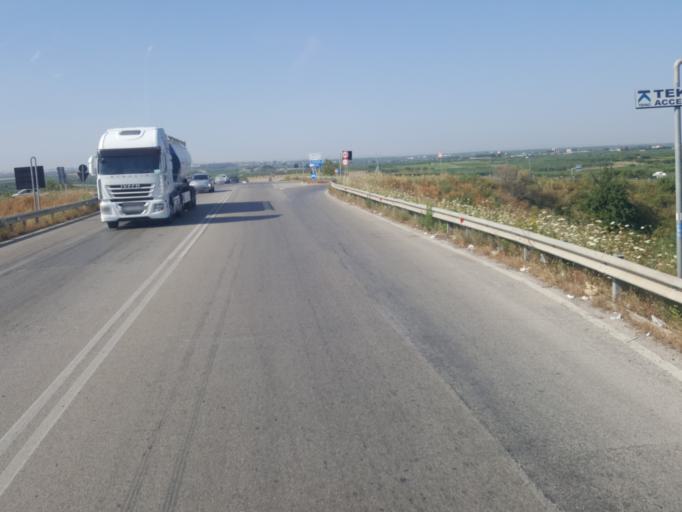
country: IT
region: Apulia
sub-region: Provincia di Barletta - Andria - Trani
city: Barletta
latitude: 41.3045
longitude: 16.3103
